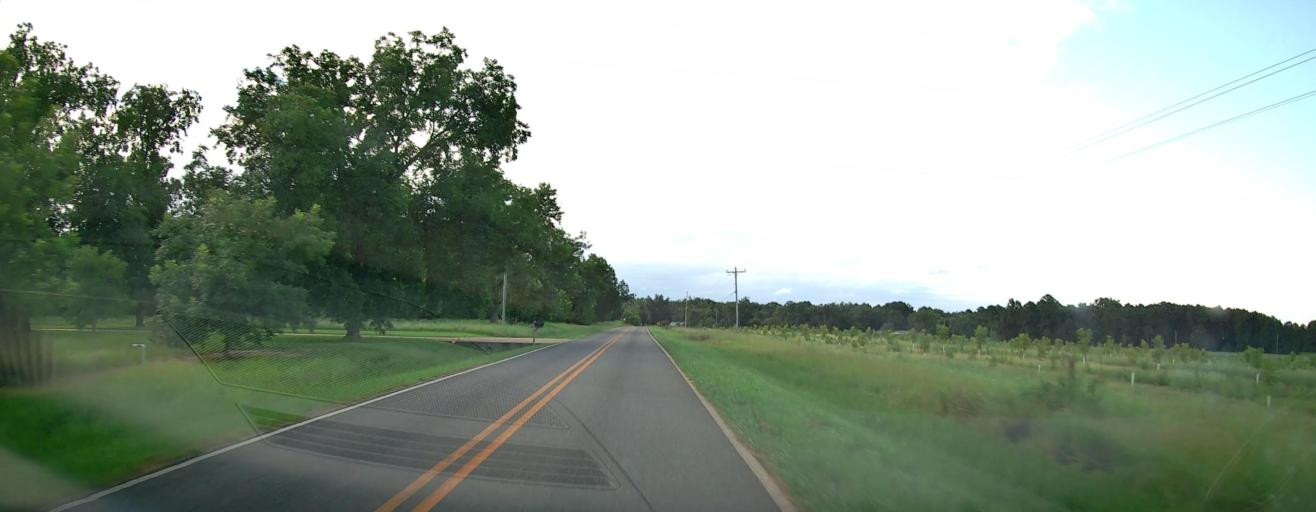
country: US
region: Georgia
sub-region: Pulaski County
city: Hawkinsville
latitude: 32.3192
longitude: -83.5523
